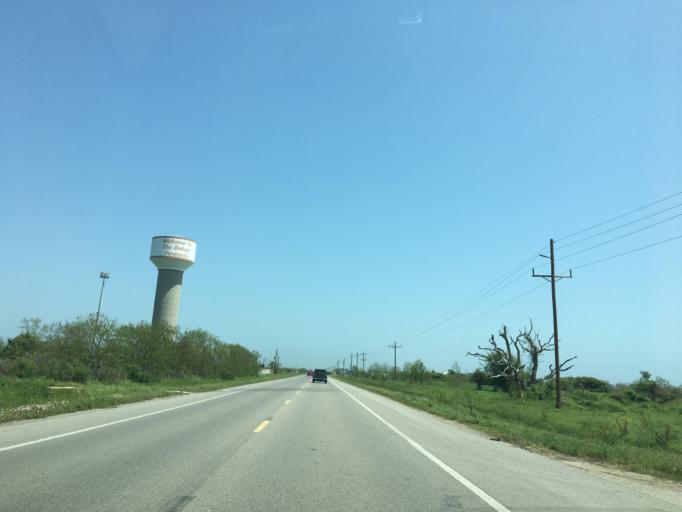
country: US
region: Texas
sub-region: Galveston County
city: Bolivar Peninsula
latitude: 29.4204
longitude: -94.7036
